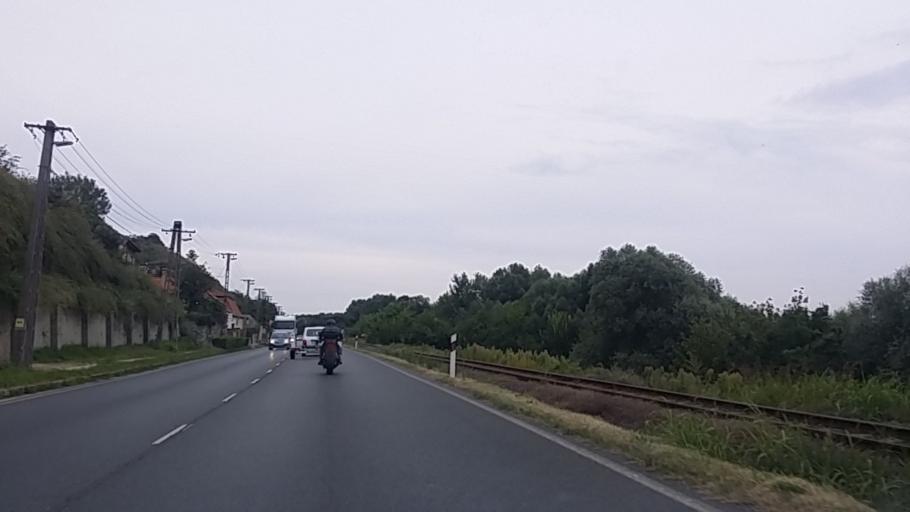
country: HU
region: Tolna
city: Paks
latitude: 46.6328
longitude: 18.8751
